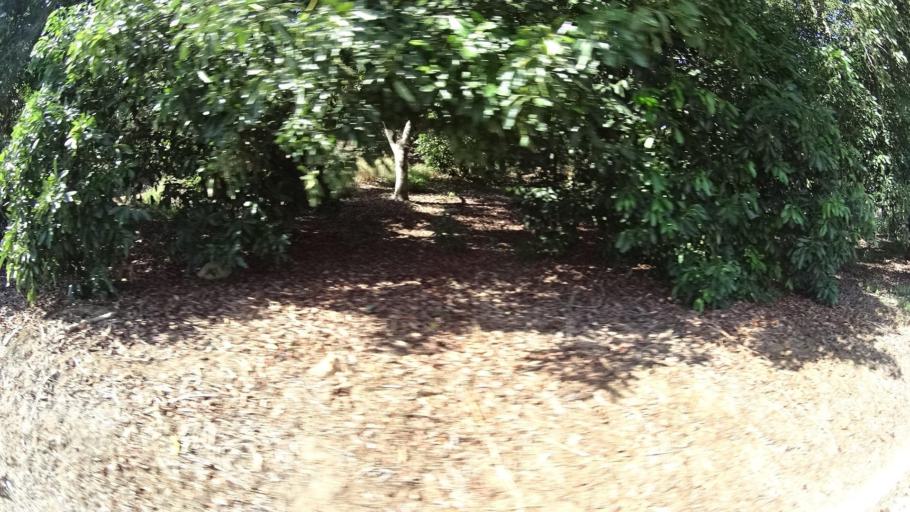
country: US
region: California
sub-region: San Diego County
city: Valley Center
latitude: 33.3074
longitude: -117.0499
